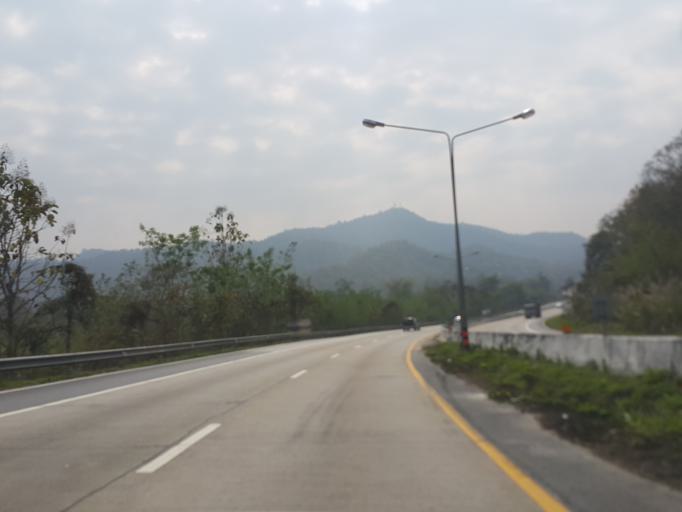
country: TH
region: Lamphun
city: Mae Tha
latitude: 18.4524
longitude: 99.2024
